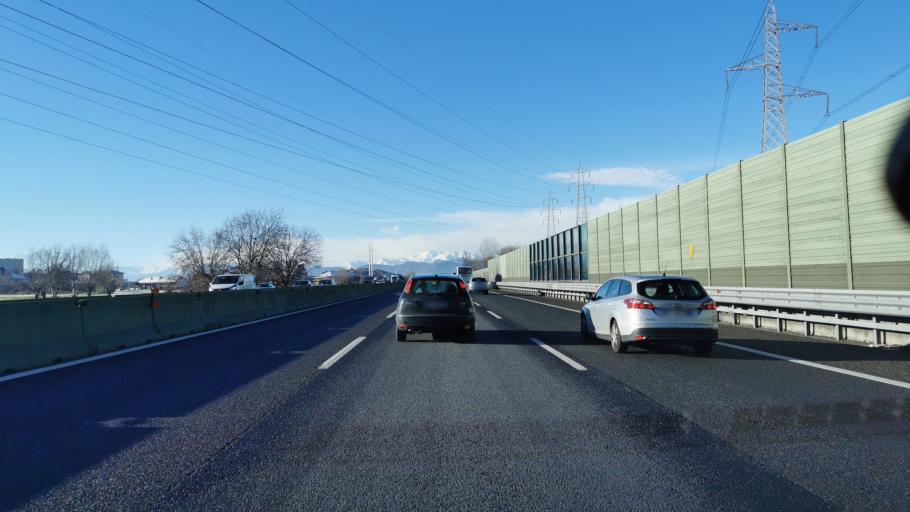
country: IT
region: Piedmont
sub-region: Provincia di Torino
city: Savonera
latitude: 45.1124
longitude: 7.6177
